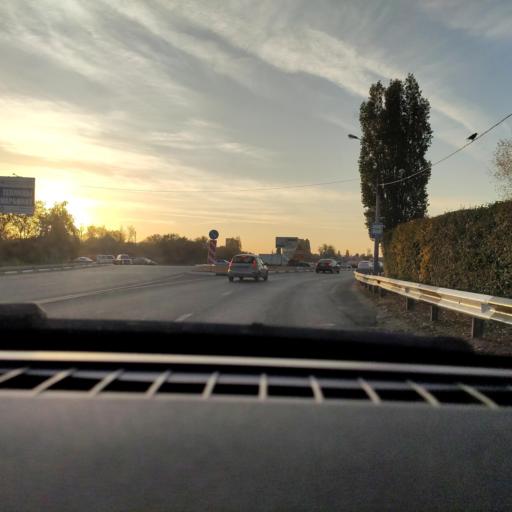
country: RU
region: Voronezj
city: Voronezh
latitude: 51.6653
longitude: 39.2686
